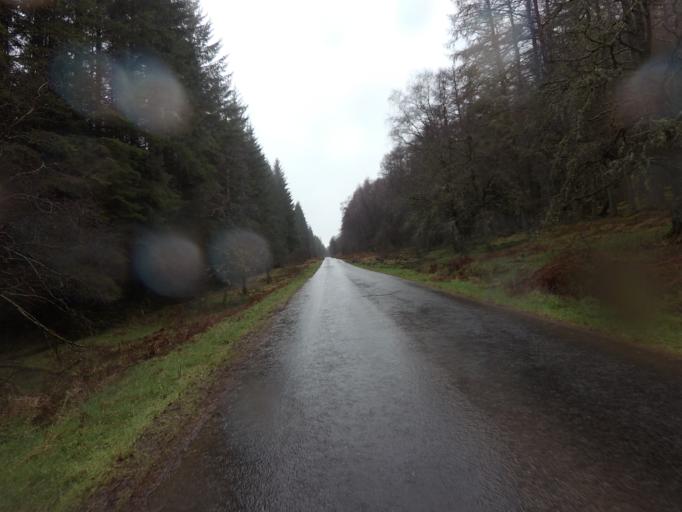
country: GB
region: Scotland
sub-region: West Dunbartonshire
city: Balloch
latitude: 56.2281
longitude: -4.5554
